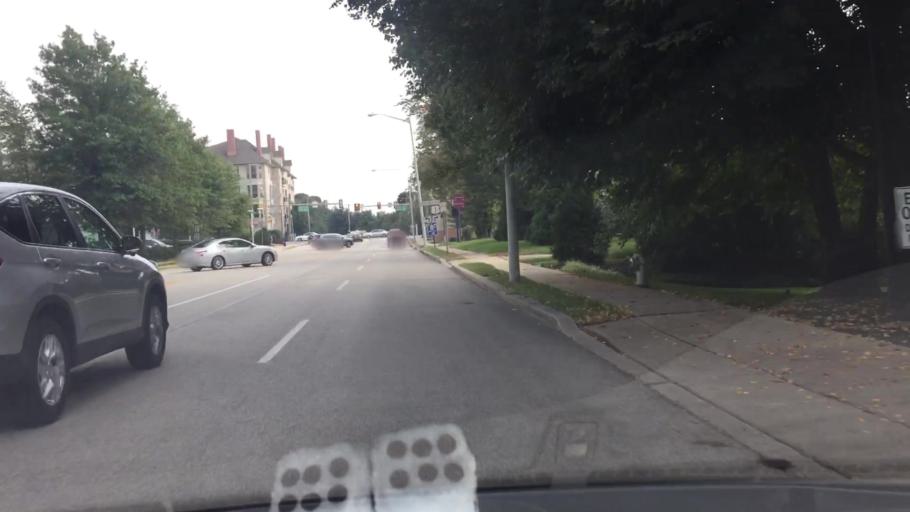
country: US
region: Pennsylvania
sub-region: Montgomery County
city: Bala-Cynwyd
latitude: 40.0024
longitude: -75.2275
